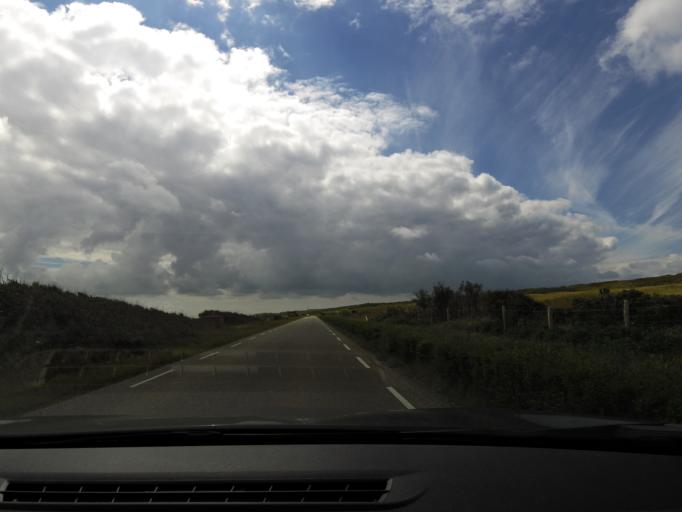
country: NL
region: Zeeland
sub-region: Gemeente Middelburg
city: Middelburg
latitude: 51.5573
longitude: 3.4807
